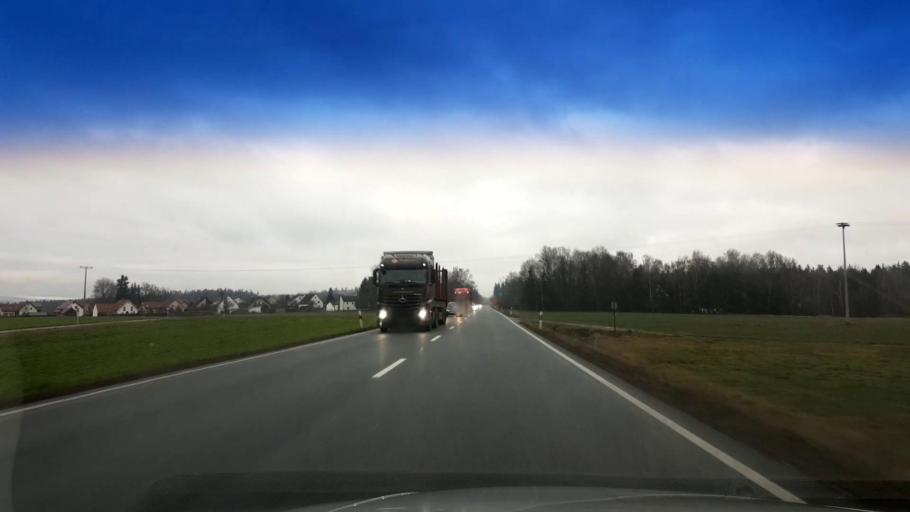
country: DE
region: Bavaria
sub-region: Upper Palatinate
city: Leonberg
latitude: 49.9320
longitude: 12.2726
